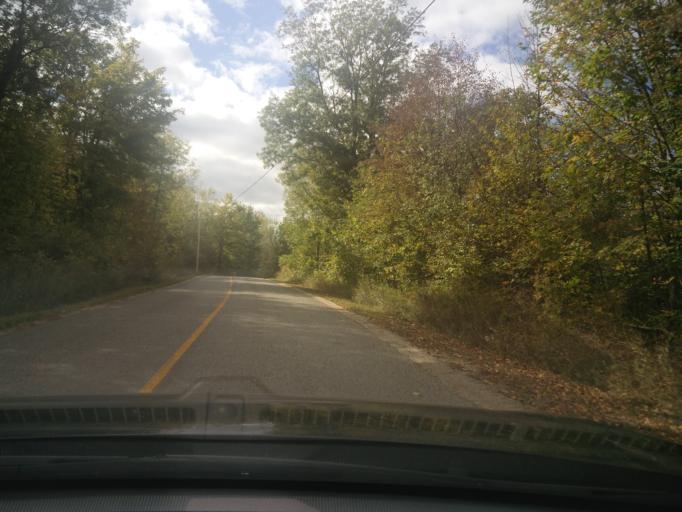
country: CA
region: Ontario
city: Perth
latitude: 44.6572
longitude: -76.5651
